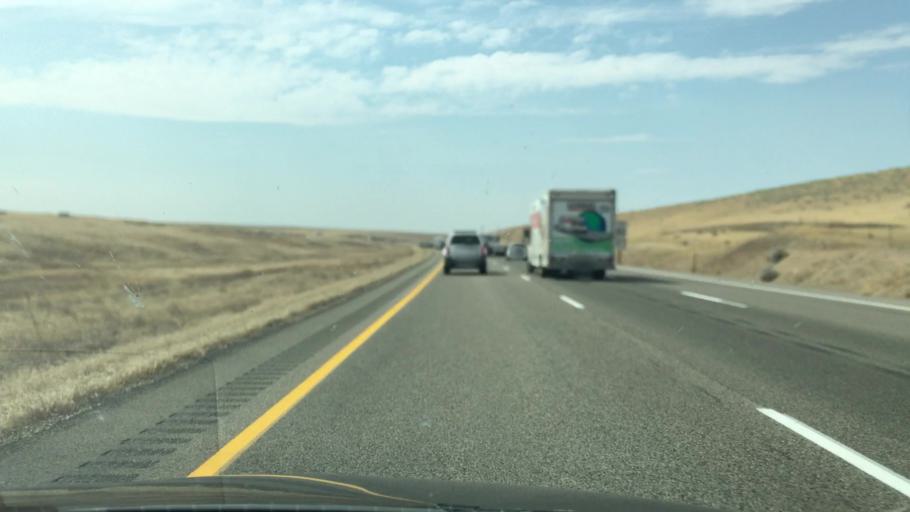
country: US
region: Idaho
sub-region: Ada County
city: Boise
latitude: 43.4823
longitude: -116.1112
